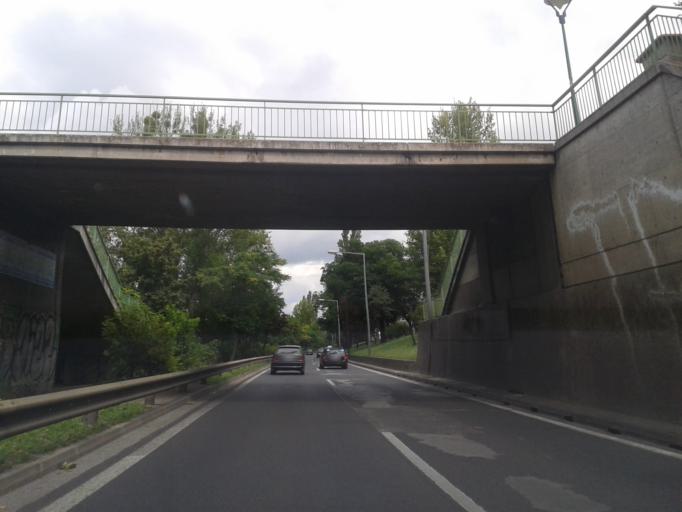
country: AT
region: Vienna
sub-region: Wien Stadt
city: Vienna
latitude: 48.2363
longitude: 16.3625
